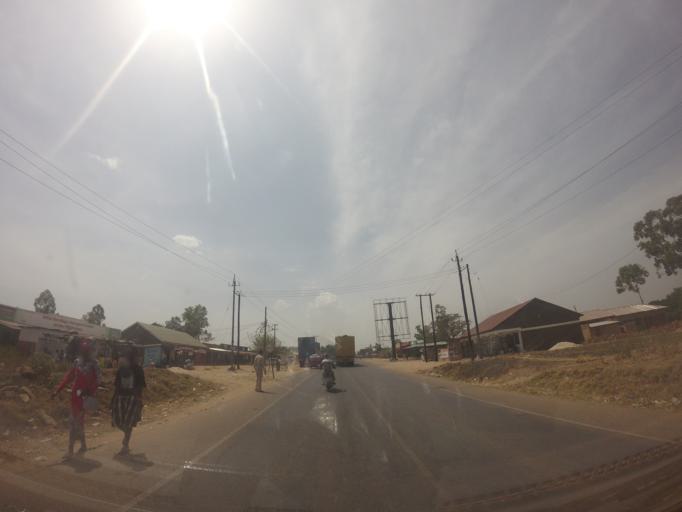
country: UG
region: Northern Region
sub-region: Arua District
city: Arua
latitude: 2.9586
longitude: 30.9167
